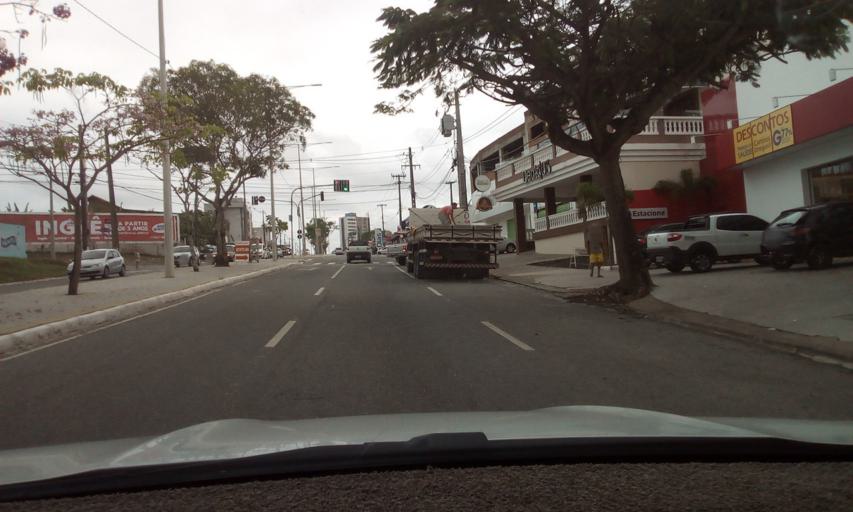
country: BR
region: Paraiba
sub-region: Campina Grande
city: Campina Grande
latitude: -7.2111
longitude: -35.8763
